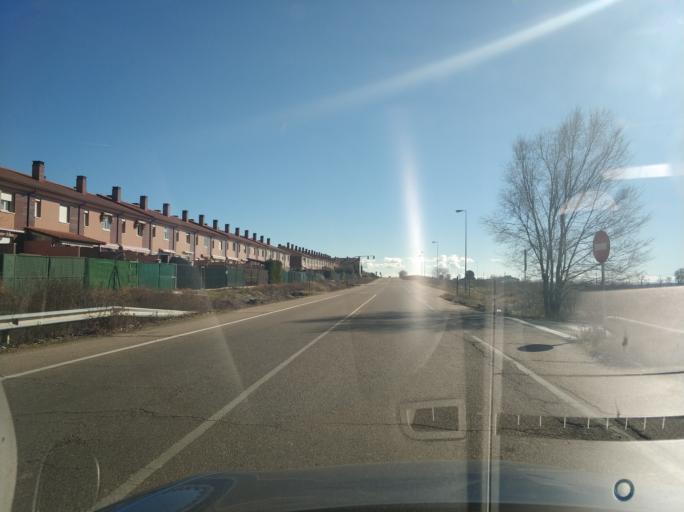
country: ES
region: Castille and Leon
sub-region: Provincia de Valladolid
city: Cisterniga
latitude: 41.6073
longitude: -4.6822
